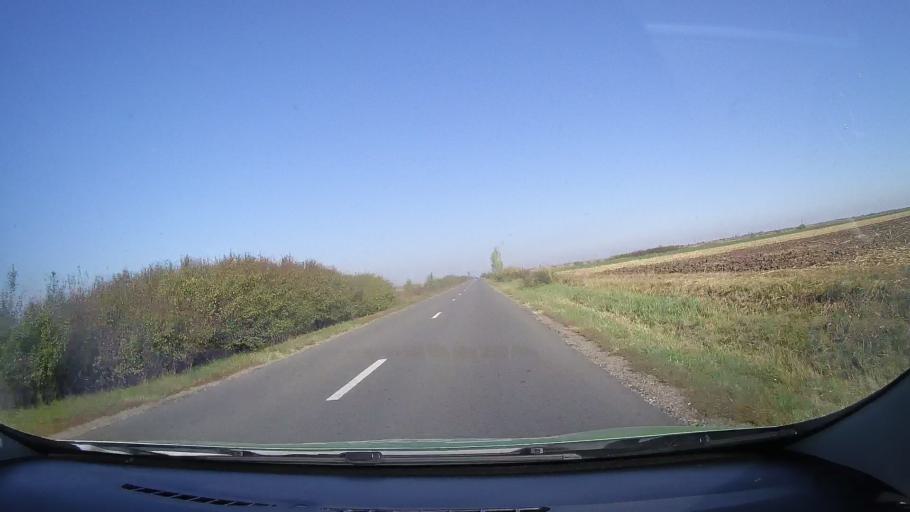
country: RO
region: Satu Mare
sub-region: Oras Tasnad
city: Tasnad
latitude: 47.5215
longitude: 22.5700
